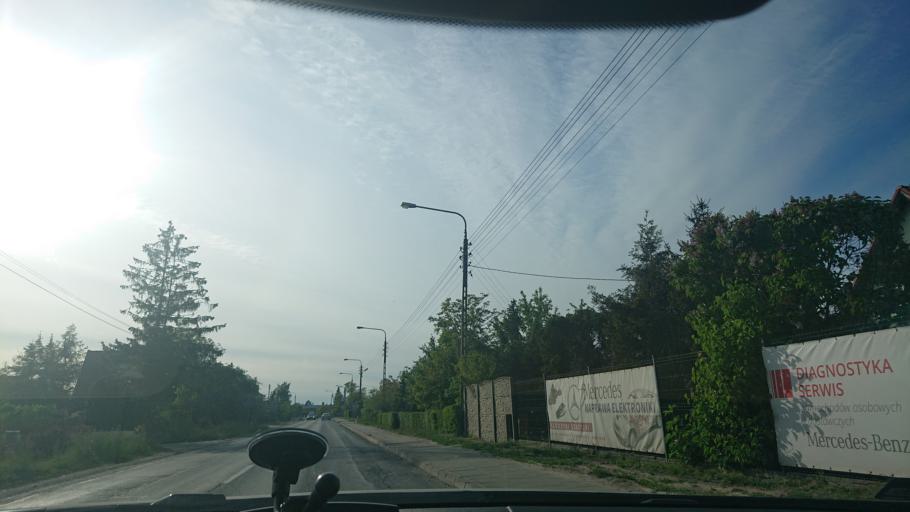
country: PL
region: Greater Poland Voivodeship
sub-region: Powiat gnieznienski
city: Gniezno
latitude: 52.5422
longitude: 17.5768
